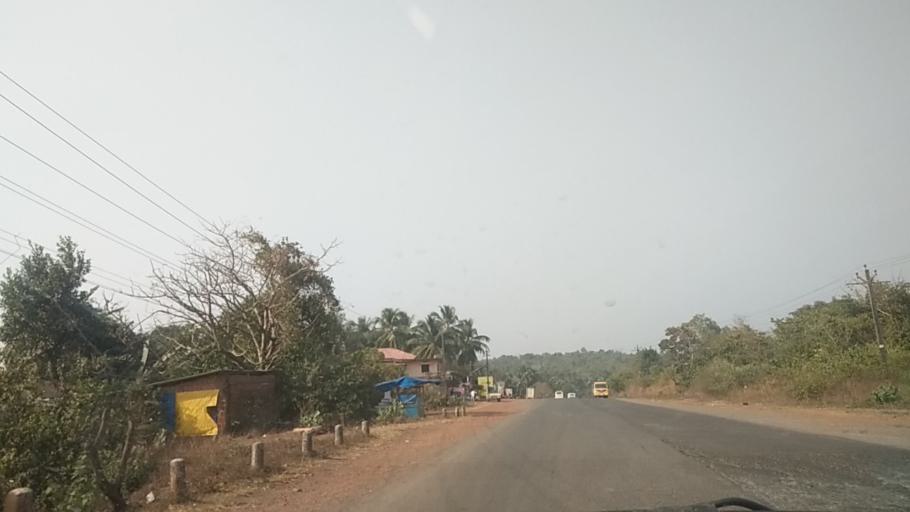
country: IN
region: Goa
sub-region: North Goa
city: Colovale
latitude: 15.6686
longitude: 73.8380
